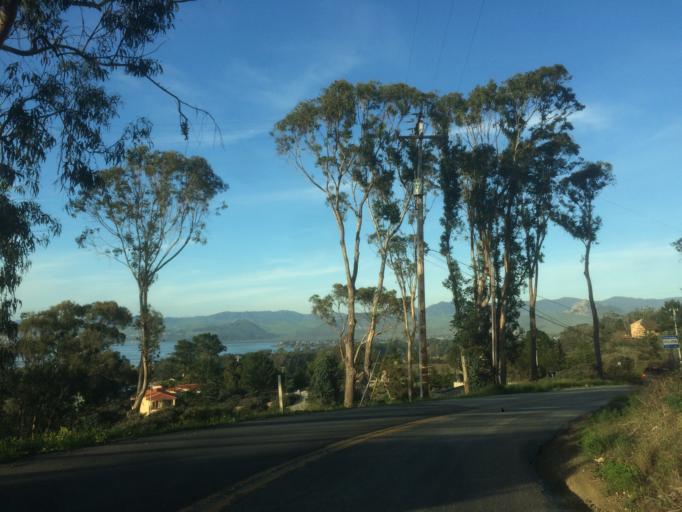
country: US
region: California
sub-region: San Luis Obispo County
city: Los Osos
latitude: 35.3011
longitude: -120.8622
